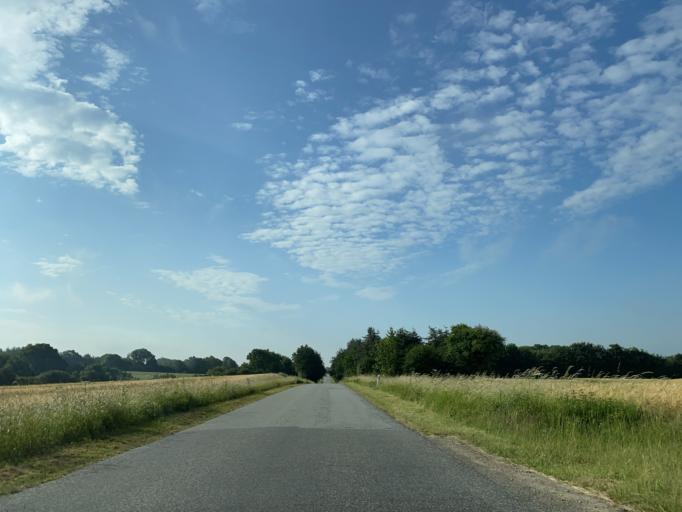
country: DK
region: South Denmark
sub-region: Haderslev Kommune
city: Haderslev
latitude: 55.1858
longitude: 9.4775
